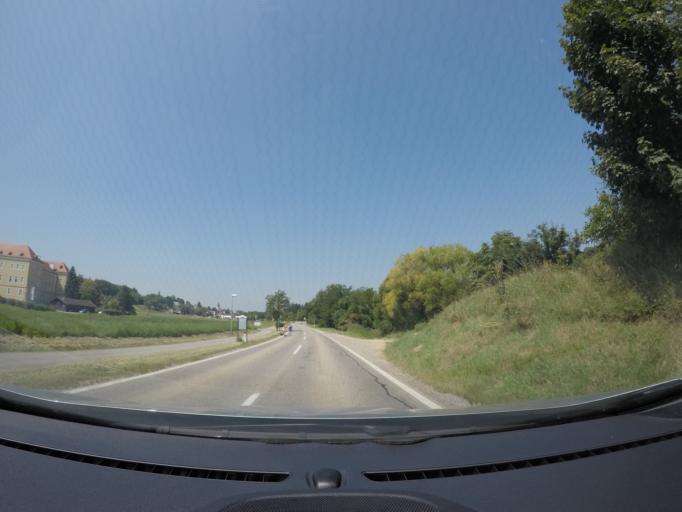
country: AT
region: Lower Austria
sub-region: Politischer Bezirk Sankt Polten
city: Maria-Anzbach
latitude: 48.1881
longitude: 15.9435
